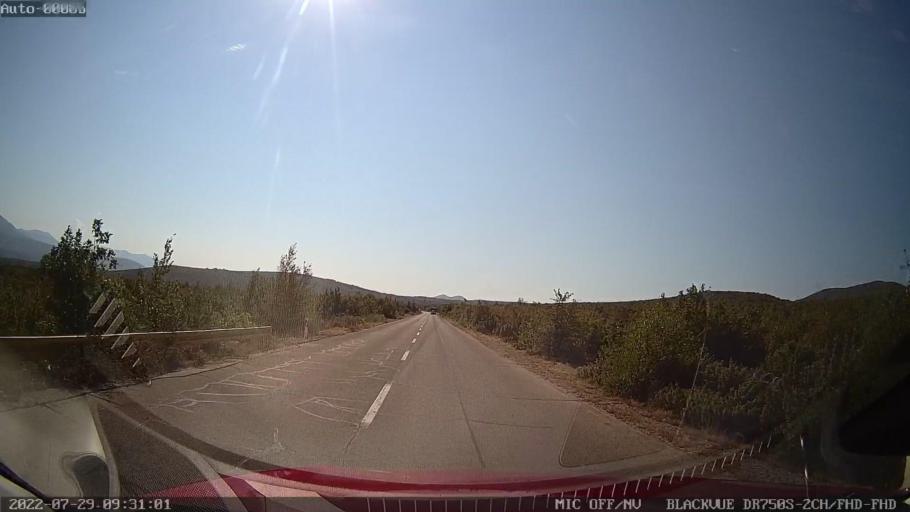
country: HR
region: Zadarska
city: Obrovac
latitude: 44.1915
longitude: 15.6937
